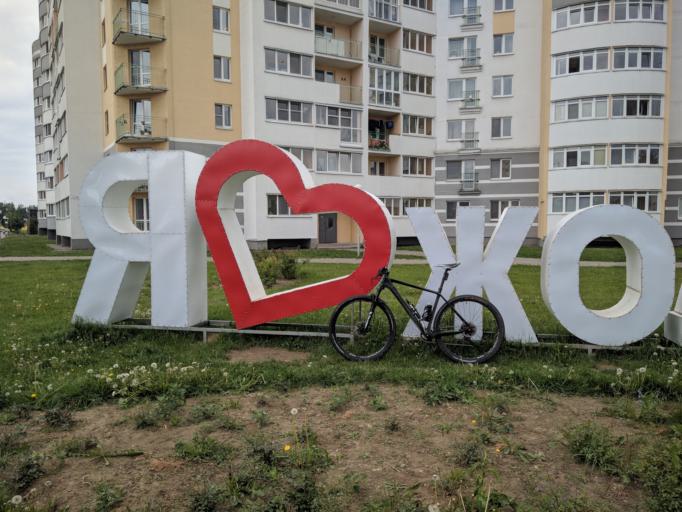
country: BY
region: Minsk
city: Horad Zhodzina
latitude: 54.0879
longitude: 28.3043
